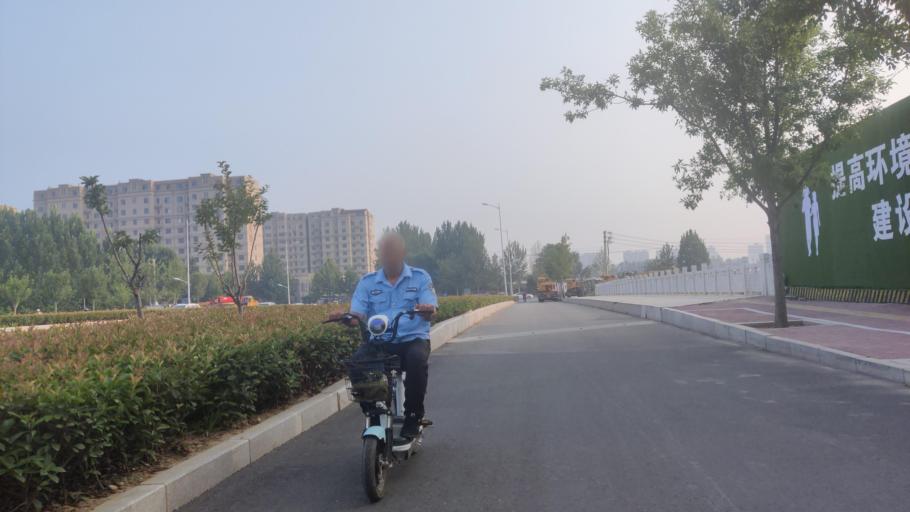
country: CN
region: Henan Sheng
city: Zhongyuanlu
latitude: 35.7579
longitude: 115.0828
